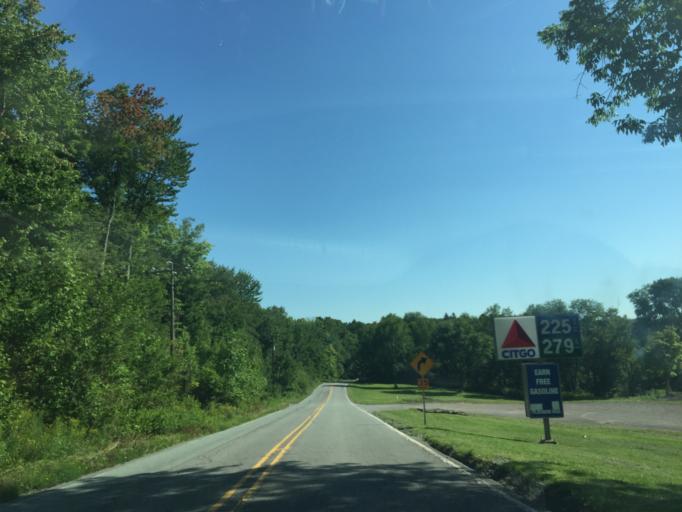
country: US
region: Pennsylvania
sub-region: Wayne County
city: Honesdale
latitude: 41.7163
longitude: -75.2286
